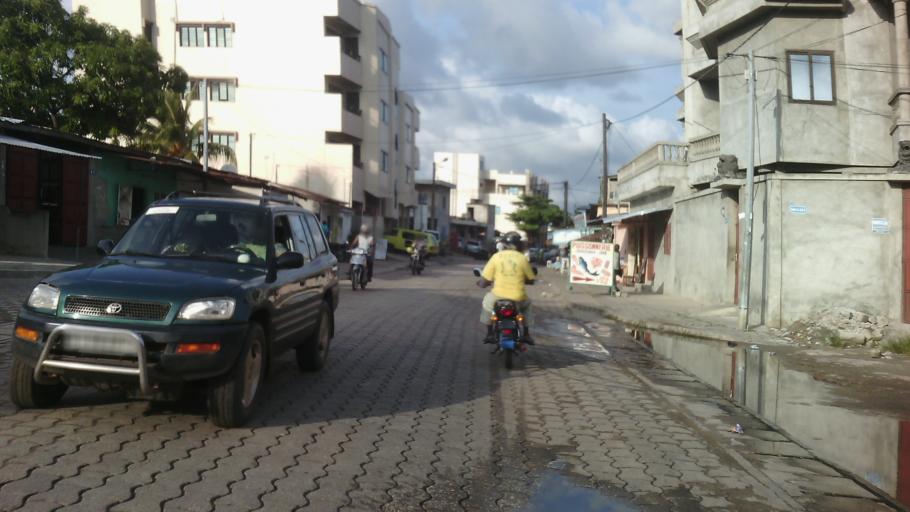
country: BJ
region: Littoral
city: Cotonou
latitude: 6.3901
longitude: 2.3665
